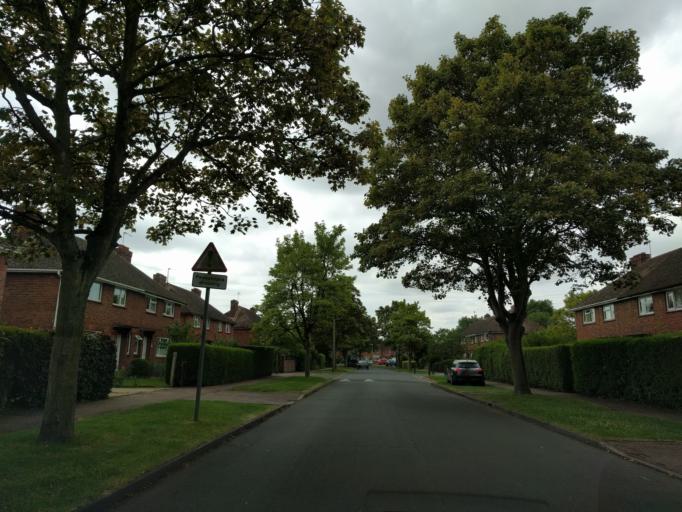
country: GB
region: England
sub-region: Cambridgeshire
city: Hemingford Grey
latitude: 52.3325
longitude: -0.0792
